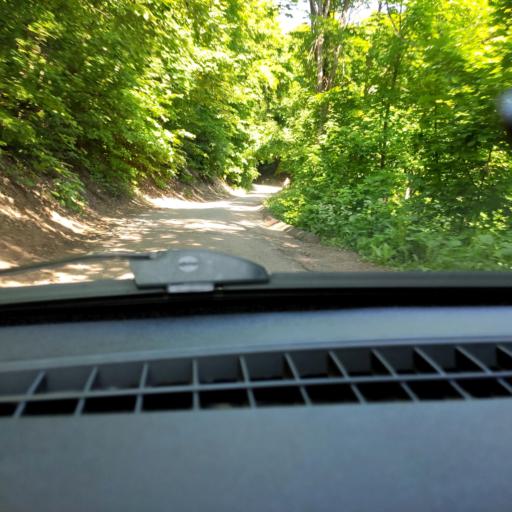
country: RU
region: Bashkortostan
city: Ufa
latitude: 54.7254
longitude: 56.0273
